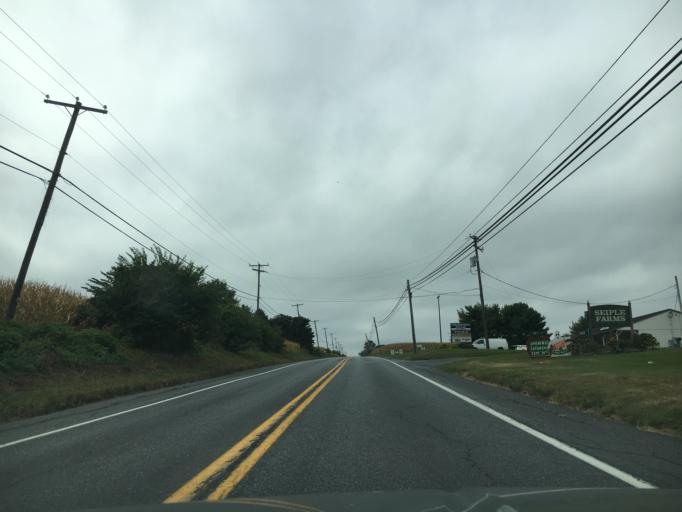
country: US
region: Pennsylvania
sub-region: Northampton County
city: Bath
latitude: 40.7031
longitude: -75.4241
